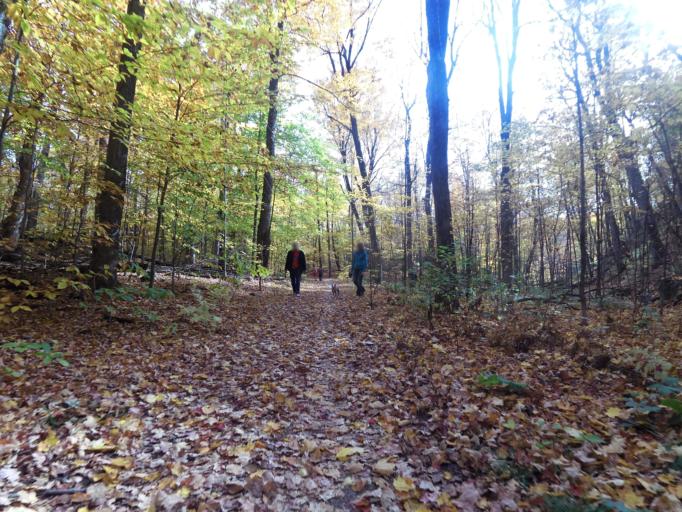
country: CA
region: Quebec
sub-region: Outaouais
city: Gatineau
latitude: 45.4754
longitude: -75.8242
